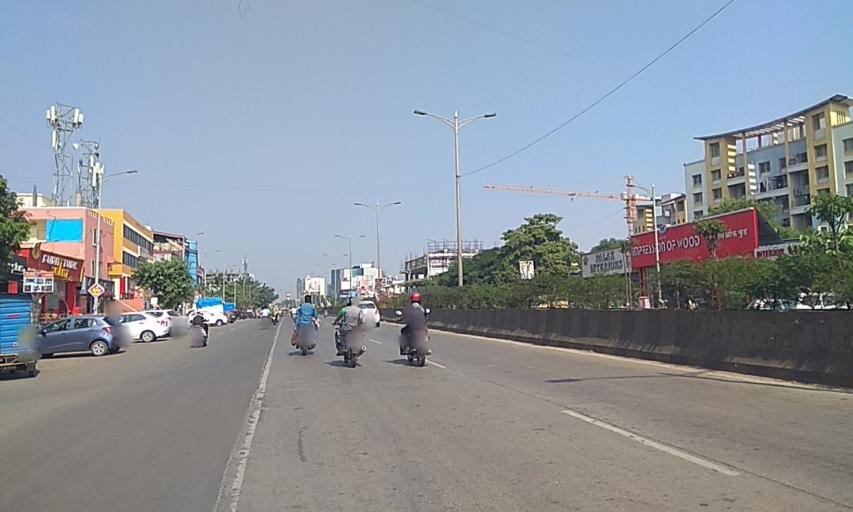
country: IN
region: Maharashtra
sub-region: Pune Division
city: Lohogaon
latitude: 18.5470
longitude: 73.9362
